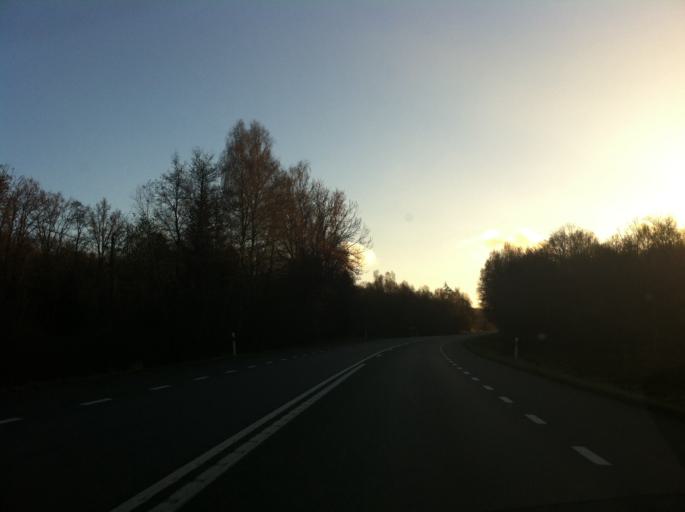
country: SE
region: Skane
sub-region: Hassleholms Kommun
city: Hassleholm
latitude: 56.1621
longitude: 13.8234
